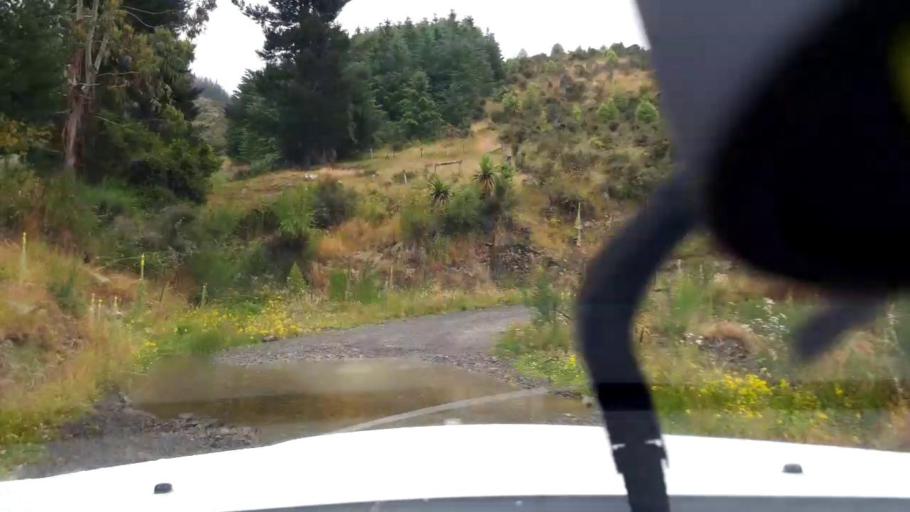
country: NZ
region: Canterbury
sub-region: Timaru District
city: Pleasant Point
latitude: -44.0457
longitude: 171.0205
